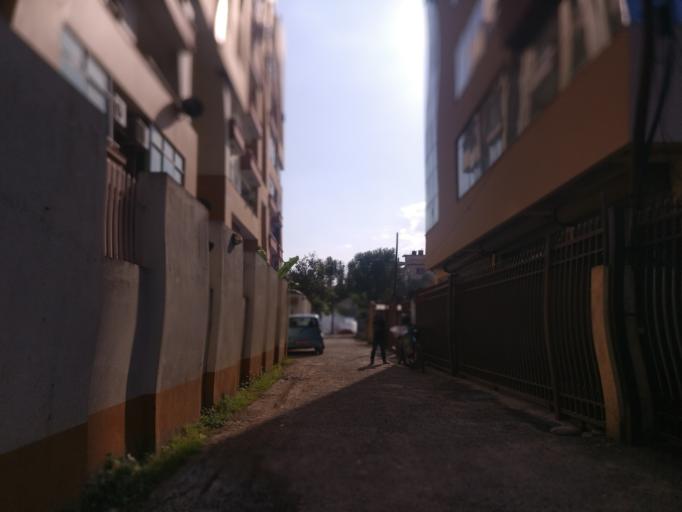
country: NP
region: Central Region
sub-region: Bagmati Zone
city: Patan
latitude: 27.6866
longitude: 85.3202
